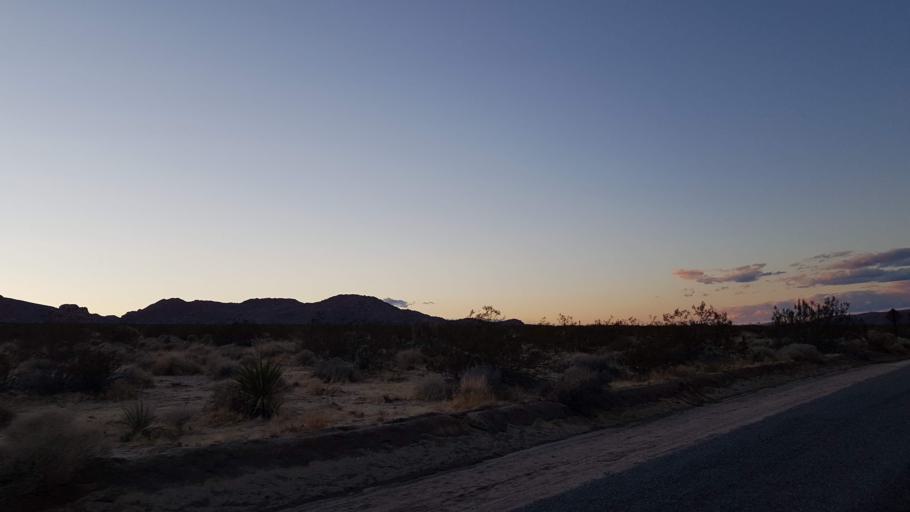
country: US
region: California
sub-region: San Bernardino County
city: Twentynine Palms
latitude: 34.1083
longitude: -116.1525
